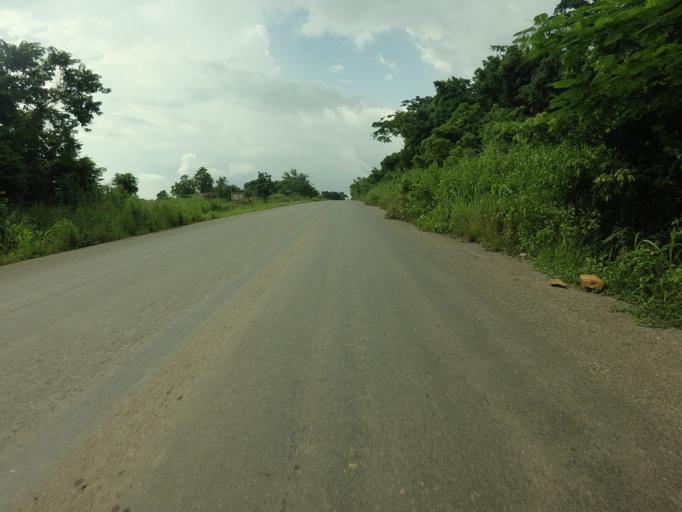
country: GH
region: Volta
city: Kpandu
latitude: 6.8793
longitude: 0.4207
